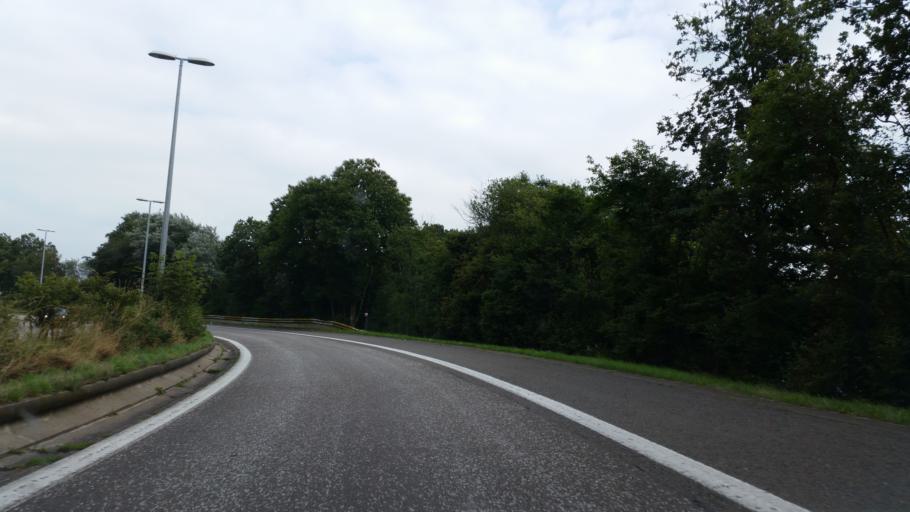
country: BE
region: Flanders
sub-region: Provincie Antwerpen
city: Turnhout
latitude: 51.2964
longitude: 4.9480
